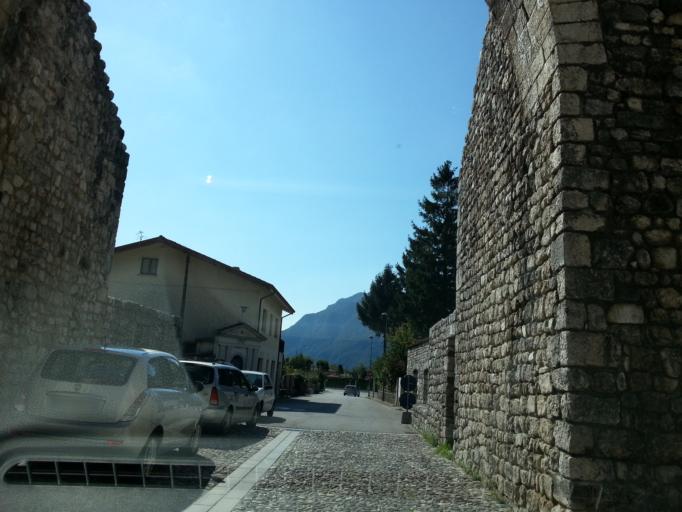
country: IT
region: Friuli Venezia Giulia
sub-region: Provincia di Udine
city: Venzone
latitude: 46.3321
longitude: 13.1391
